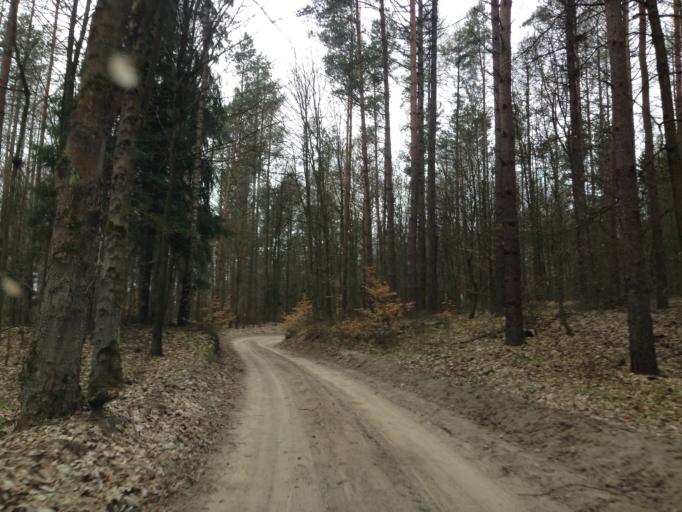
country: PL
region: Kujawsko-Pomorskie
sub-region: Powiat brodnicki
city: Gorzno
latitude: 53.2184
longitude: 19.7320
